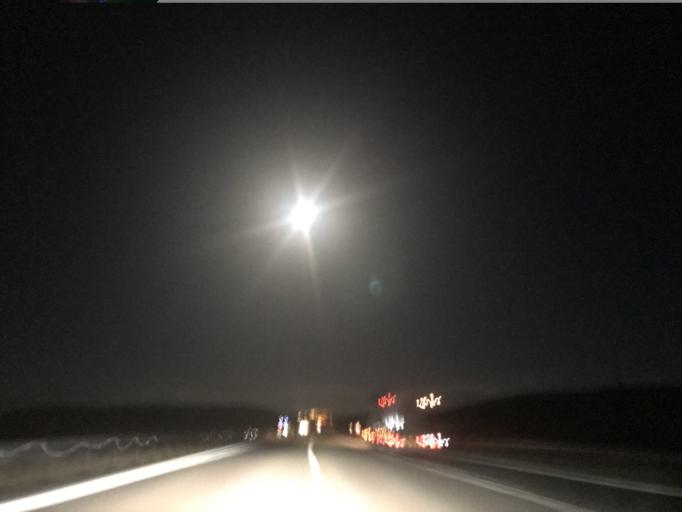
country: TR
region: Nigde
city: Ulukisla
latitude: 37.6356
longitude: 34.4352
